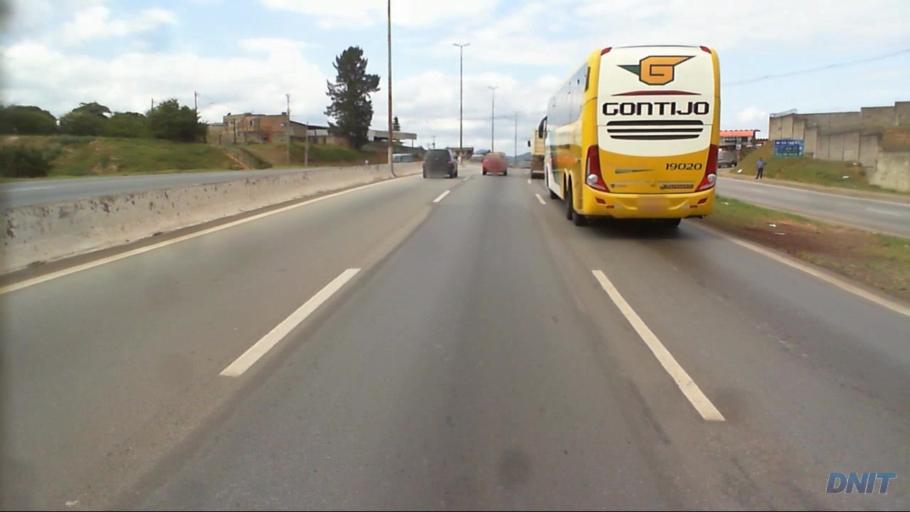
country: BR
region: Minas Gerais
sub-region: Belo Horizonte
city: Belo Horizonte
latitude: -19.8590
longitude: -43.9153
